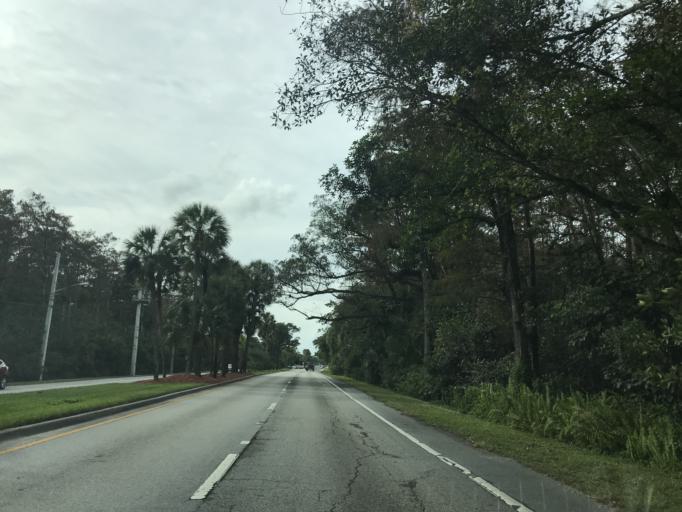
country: US
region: Florida
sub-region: Broward County
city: Coconut Creek
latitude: 26.2598
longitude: -80.1796
